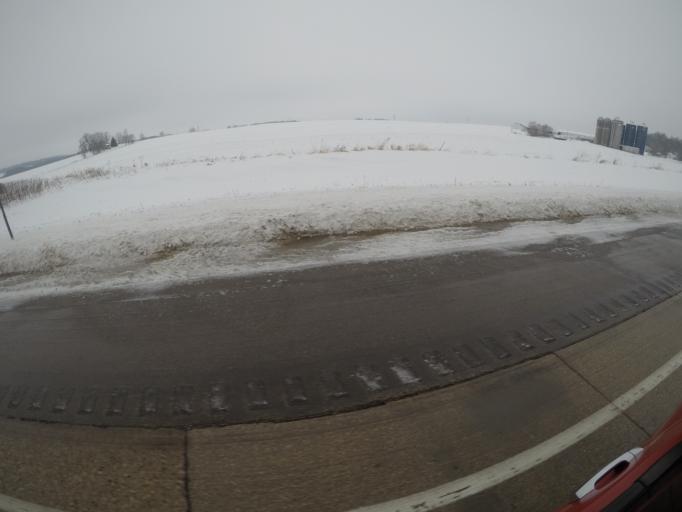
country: US
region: Minnesota
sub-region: Goodhue County
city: Zumbrota
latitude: 44.2548
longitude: -92.6507
